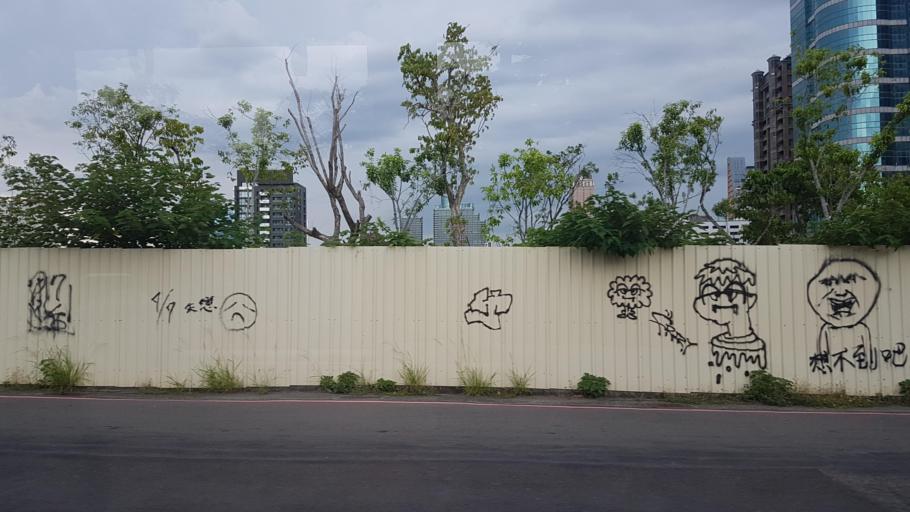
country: TW
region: Kaohsiung
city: Kaohsiung
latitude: 22.6104
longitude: 120.2986
